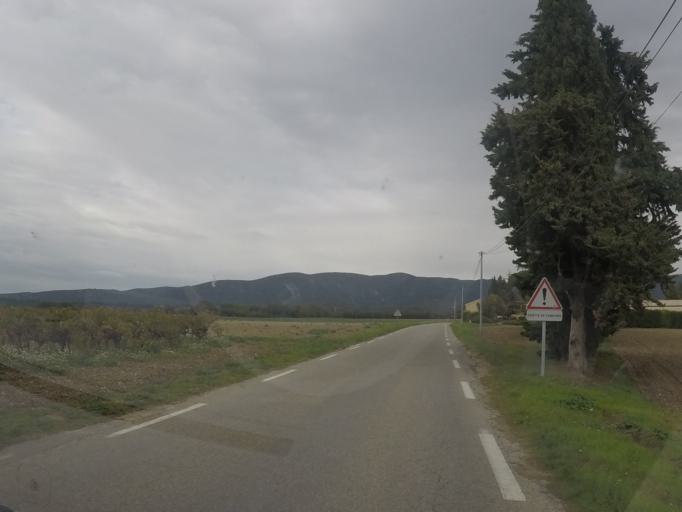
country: FR
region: Provence-Alpes-Cote d'Azur
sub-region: Departement du Vaucluse
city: Cadenet
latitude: 43.7513
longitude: 5.4036
